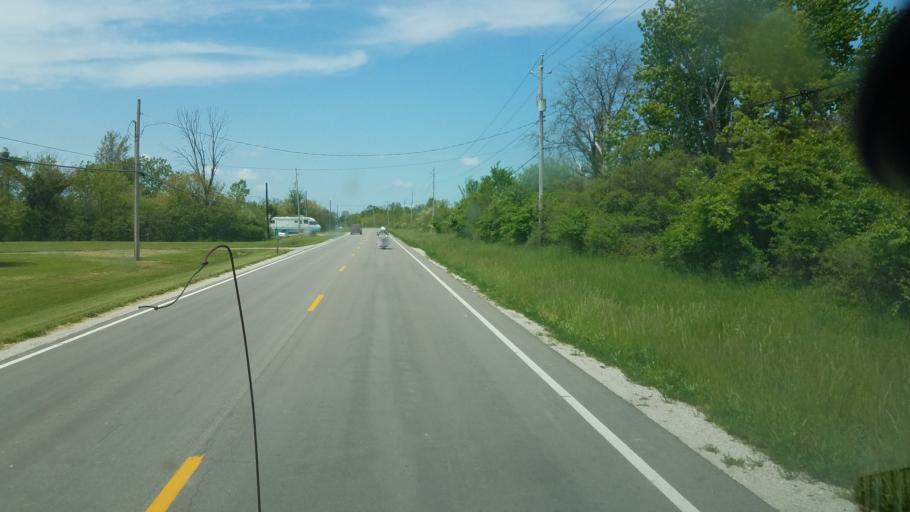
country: US
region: Ohio
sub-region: Ottawa County
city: Port Clinton
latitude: 41.5238
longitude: -83.0036
